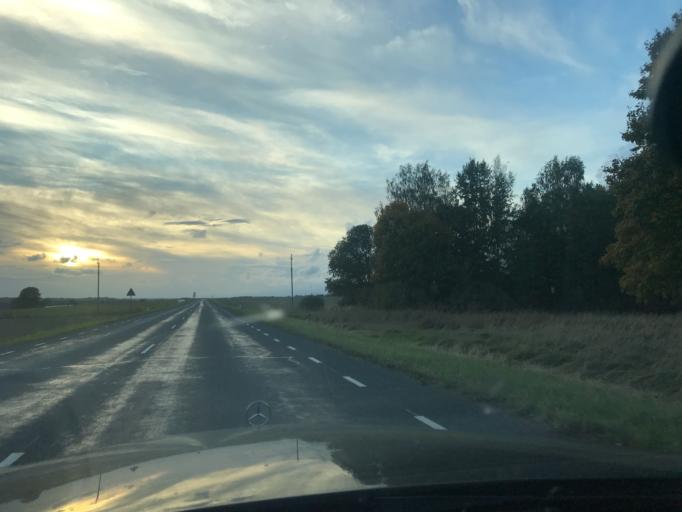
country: EE
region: Vorumaa
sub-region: Antsla vald
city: Vana-Antsla
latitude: 57.9162
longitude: 26.3699
